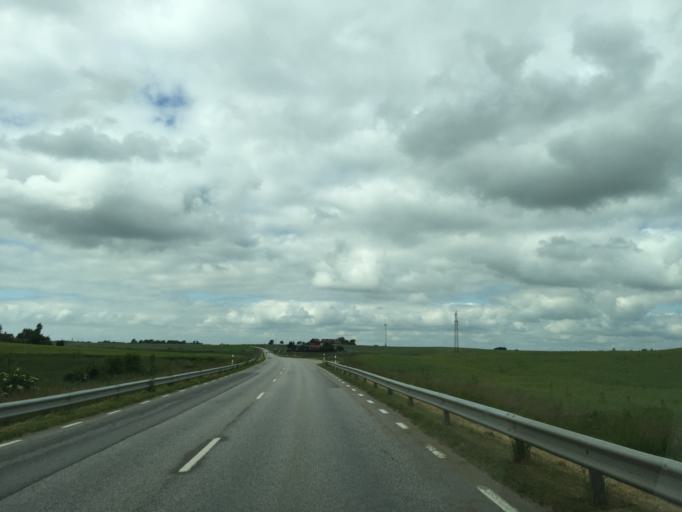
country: SE
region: Skane
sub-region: Svedala Kommun
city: Klagerup
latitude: 55.6128
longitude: 13.2643
